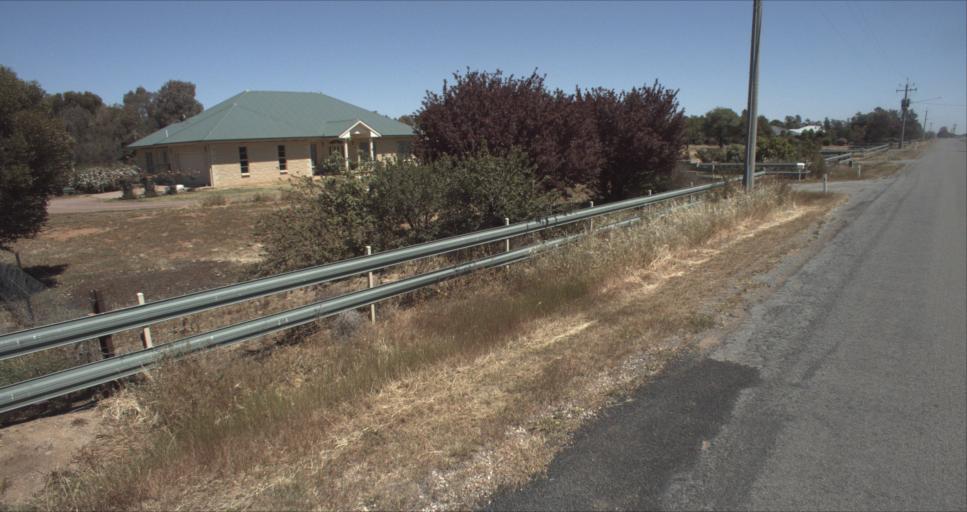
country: AU
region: New South Wales
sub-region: Leeton
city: Leeton
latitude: -34.5279
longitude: 146.3982
